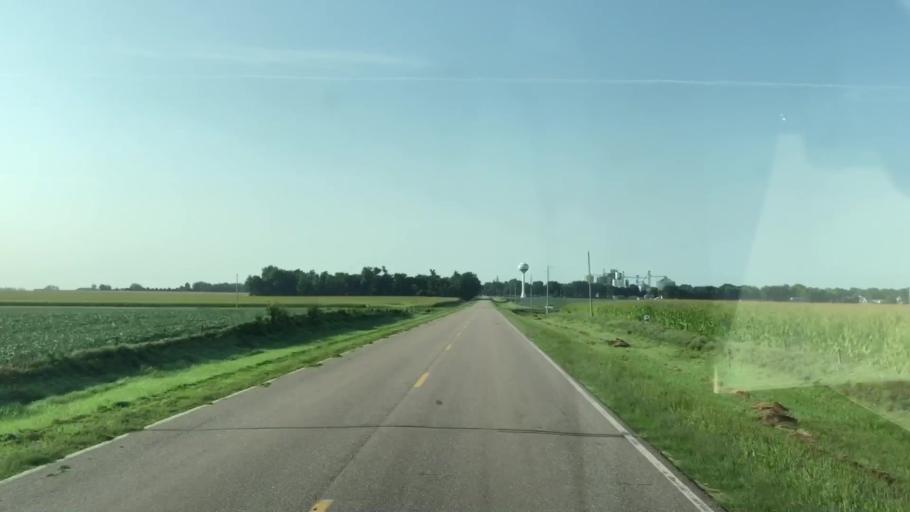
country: US
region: Iowa
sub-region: Sioux County
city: Hull
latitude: 43.2025
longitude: -96.0005
